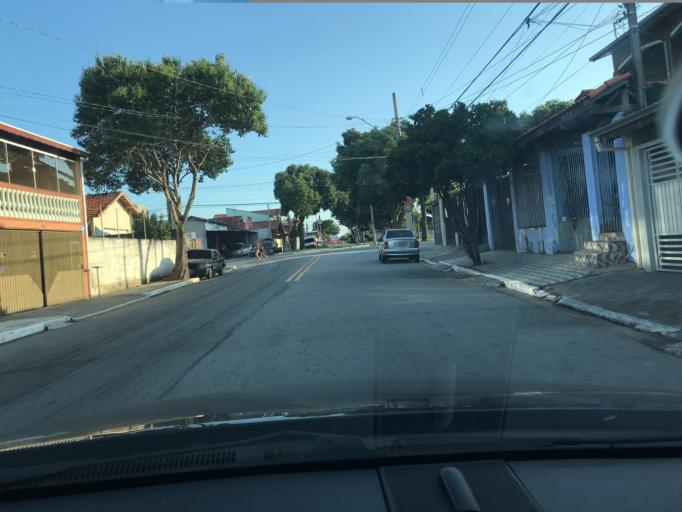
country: BR
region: Sao Paulo
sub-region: Sao Jose Dos Campos
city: Sao Jose dos Campos
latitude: -23.2602
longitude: -45.8850
